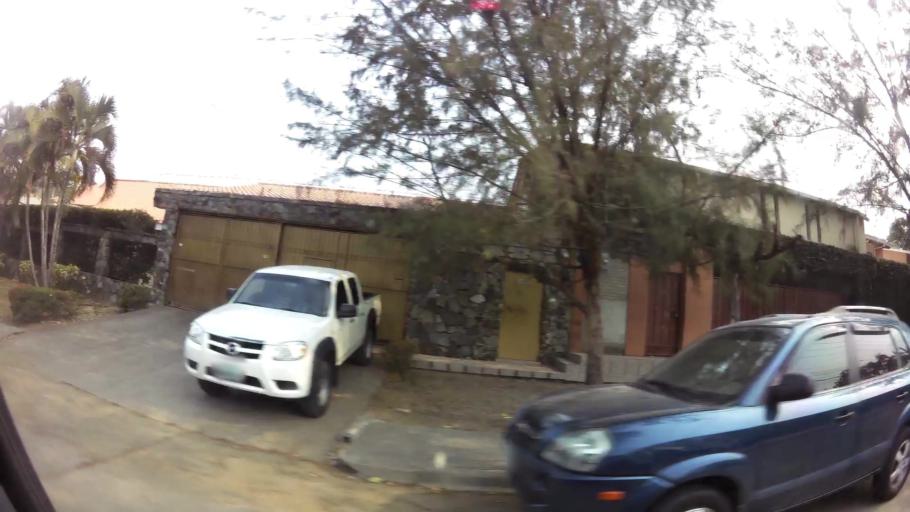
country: HN
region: Cortes
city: El Zapotal del Norte
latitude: 15.5107
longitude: -88.0401
